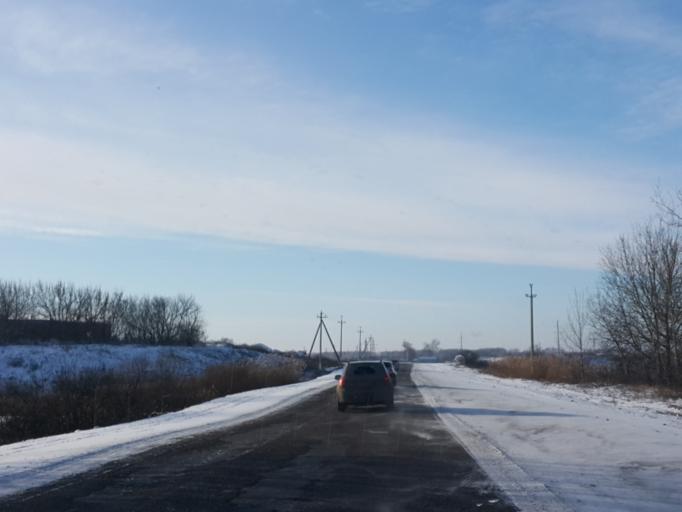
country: RU
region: Tambov
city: Znamenka
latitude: 52.4102
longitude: 41.4718
